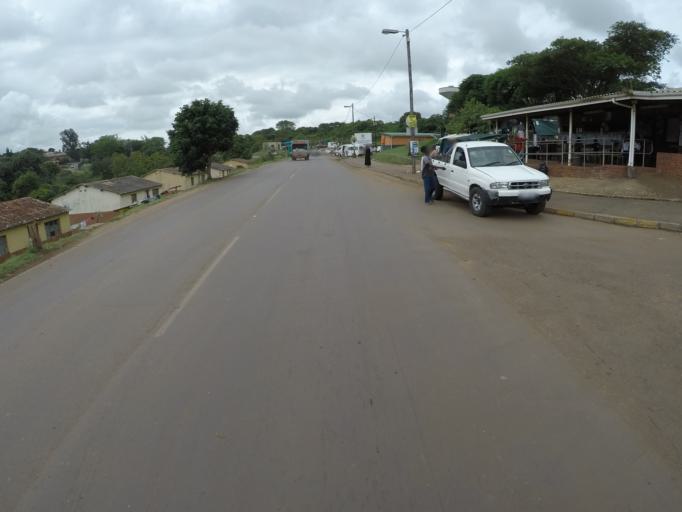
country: ZA
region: KwaZulu-Natal
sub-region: uThungulu District Municipality
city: Empangeni
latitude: -28.7776
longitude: 31.8646
